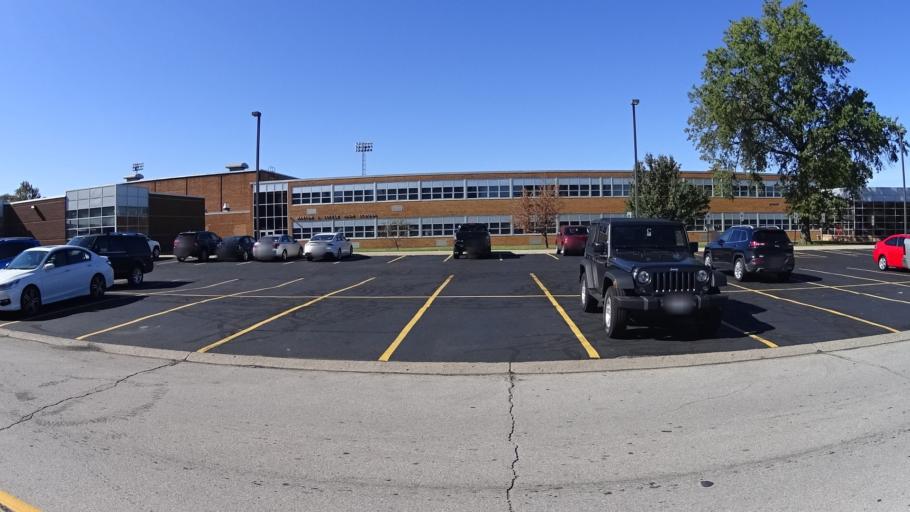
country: US
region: Ohio
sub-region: Lorain County
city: Amherst
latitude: 41.4037
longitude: -82.2216
